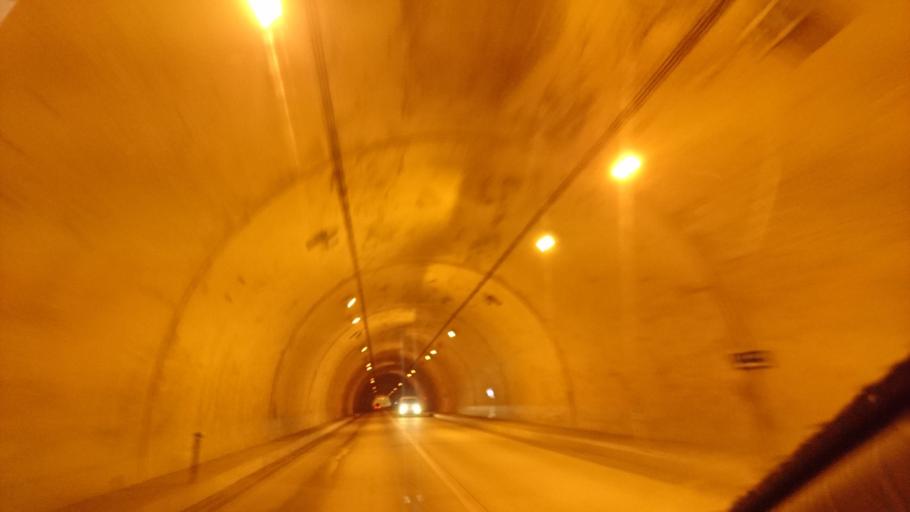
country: JP
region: Iwate
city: Mizusawa
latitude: 39.1210
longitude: 140.9056
